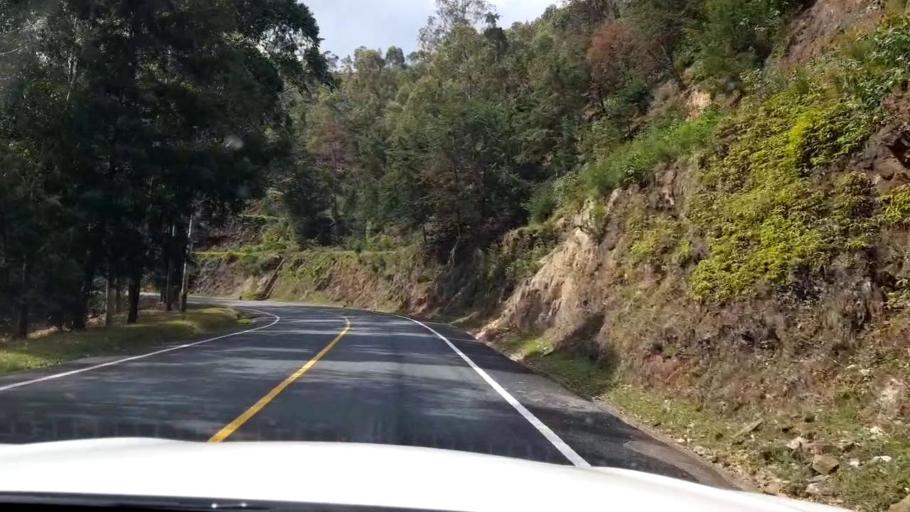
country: RW
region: Southern Province
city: Gitarama
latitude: -2.0324
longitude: 29.7185
